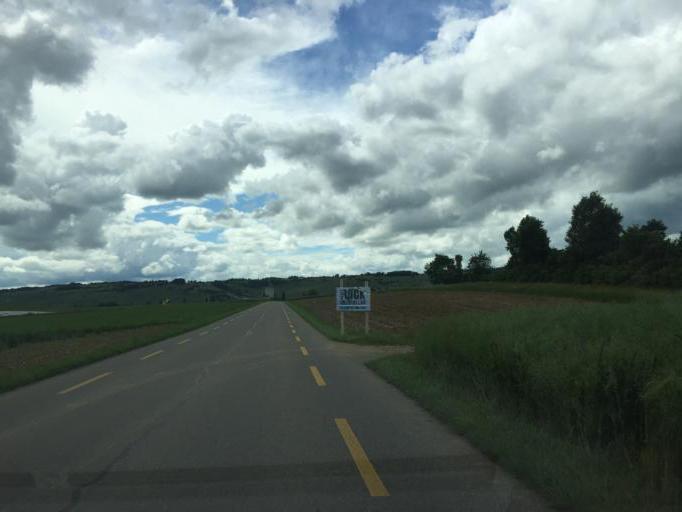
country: CH
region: Schaffhausen
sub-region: Bezirk Oberklettgau
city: Neunkirch
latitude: 47.6916
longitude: 8.4822
